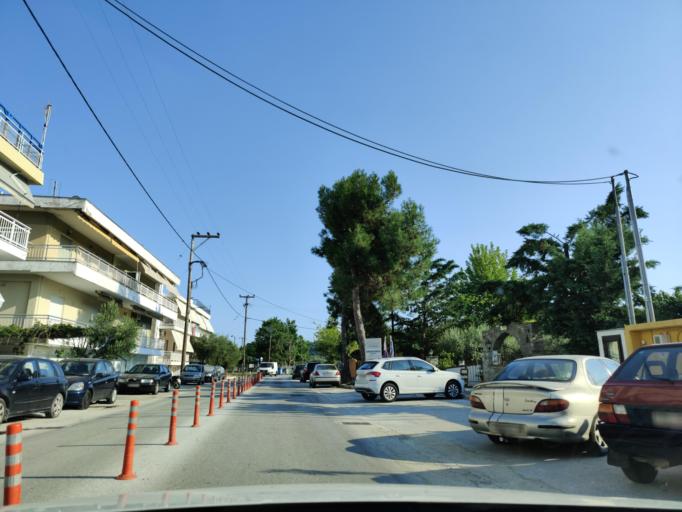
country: GR
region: East Macedonia and Thrace
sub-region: Nomos Kavalas
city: Nea Peramos
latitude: 40.8314
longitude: 24.3047
